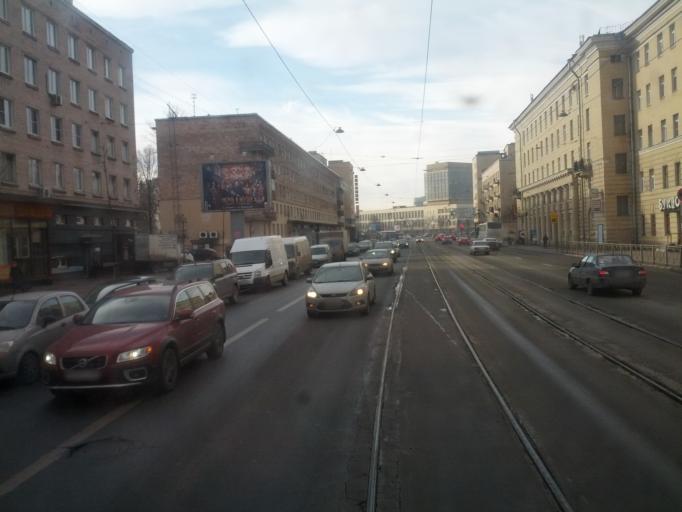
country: RU
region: Leningrad
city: Finlyandskiy
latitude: 59.9453
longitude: 30.4138
